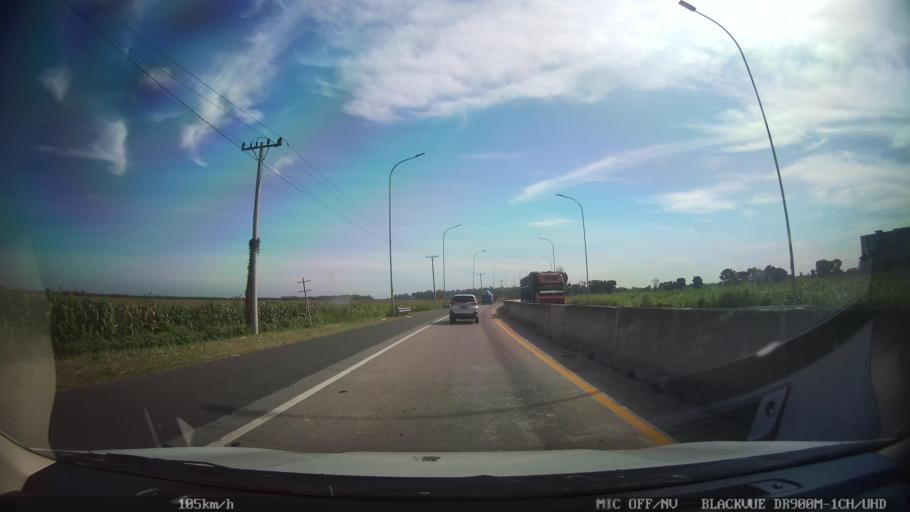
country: ID
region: North Sumatra
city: Sunggal
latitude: 3.6266
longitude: 98.6277
